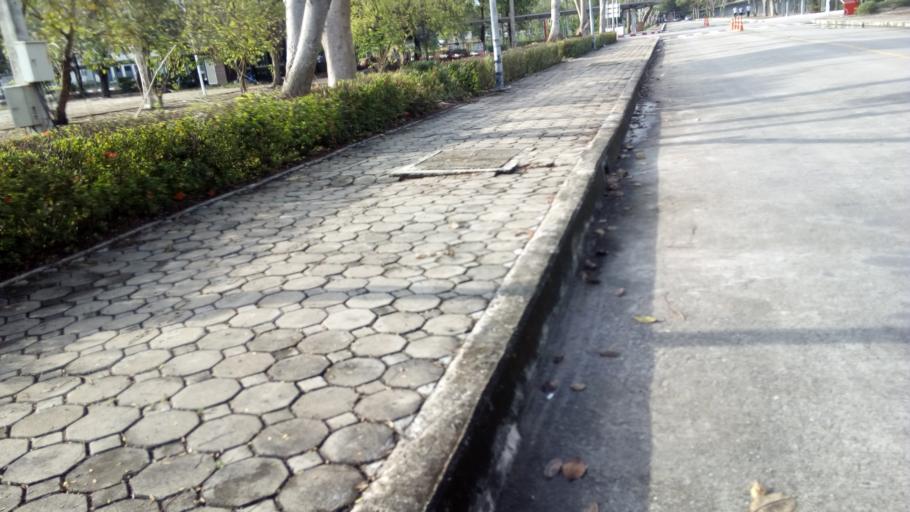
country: TH
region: Nakhon Nayok
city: Ongkharak
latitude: 14.1055
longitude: 100.9868
